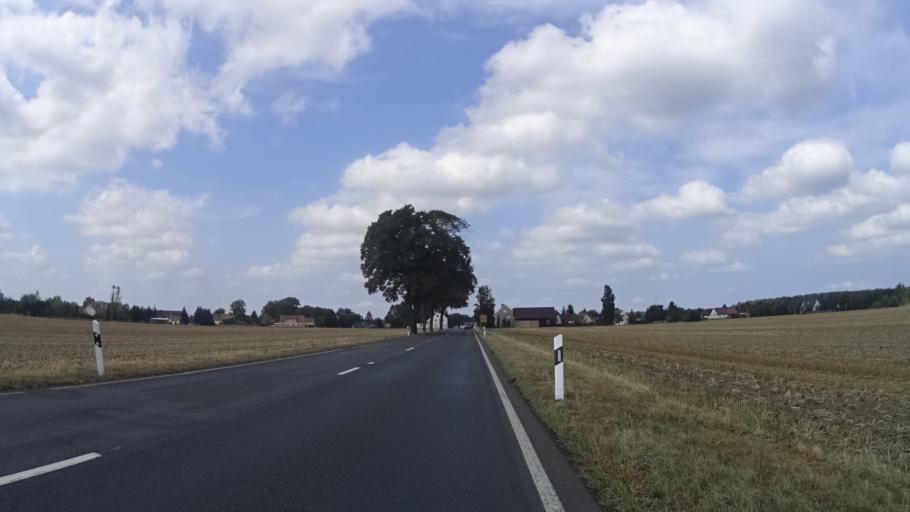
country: DE
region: Saxony
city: Gablenz
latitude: 51.5656
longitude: 14.6691
